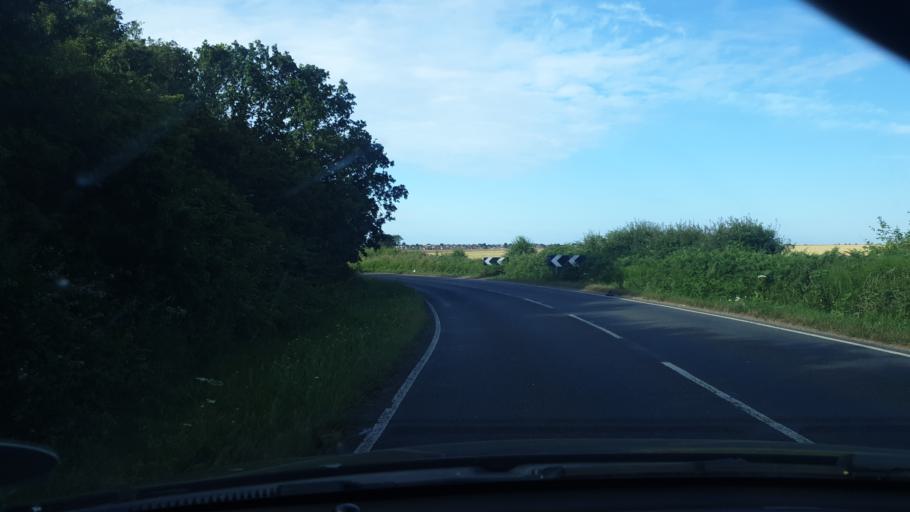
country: GB
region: England
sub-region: Essex
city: Frinton-on-Sea
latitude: 51.8193
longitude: 1.2070
